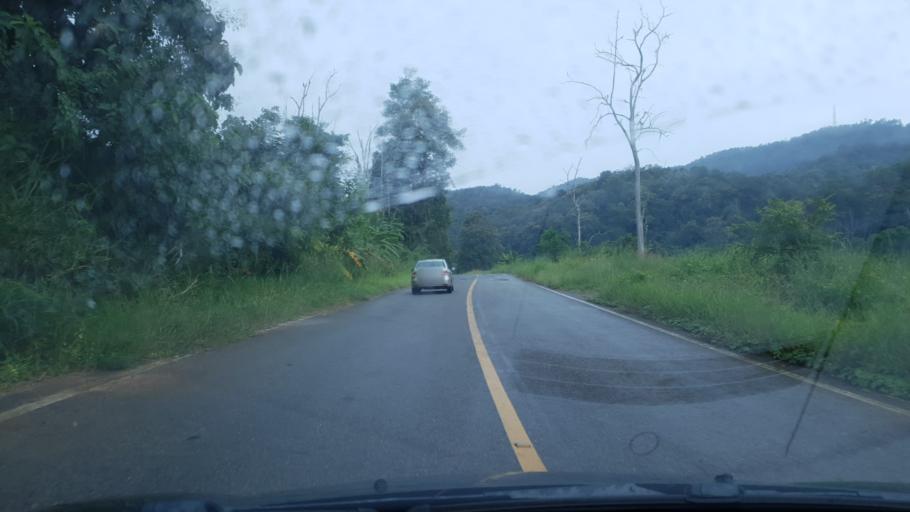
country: TH
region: Mae Hong Son
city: Khun Yuam
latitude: 18.6914
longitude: 97.9222
